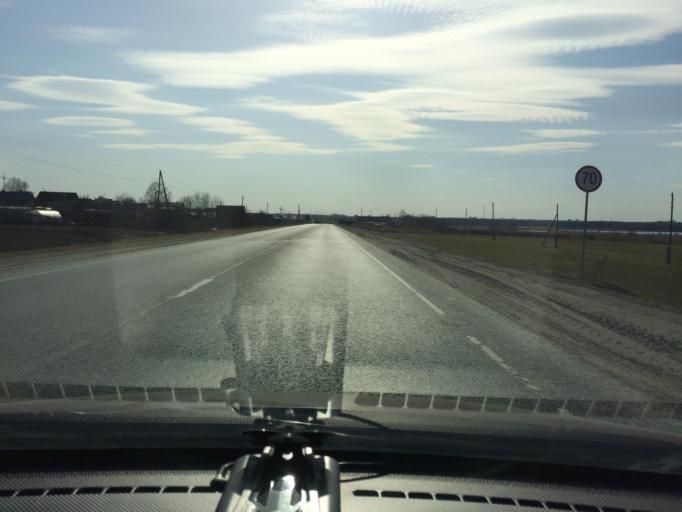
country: RU
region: Mariy-El
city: Yoshkar-Ola
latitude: 56.6612
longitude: 47.9770
